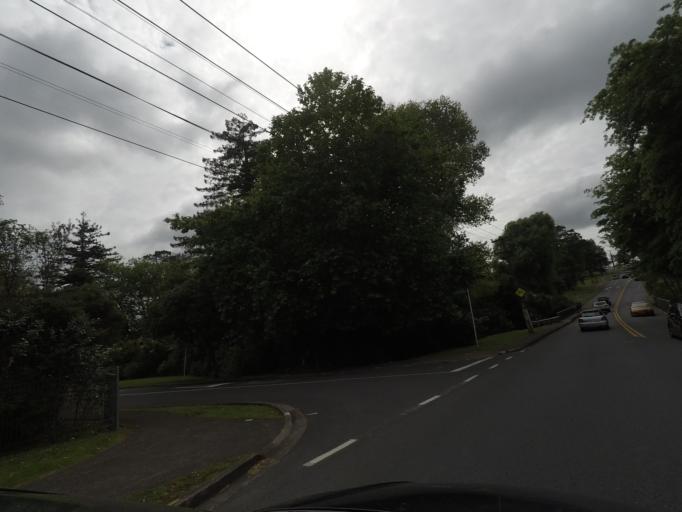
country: NZ
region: Auckland
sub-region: Auckland
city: Waitakere
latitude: -36.9046
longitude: 174.6244
